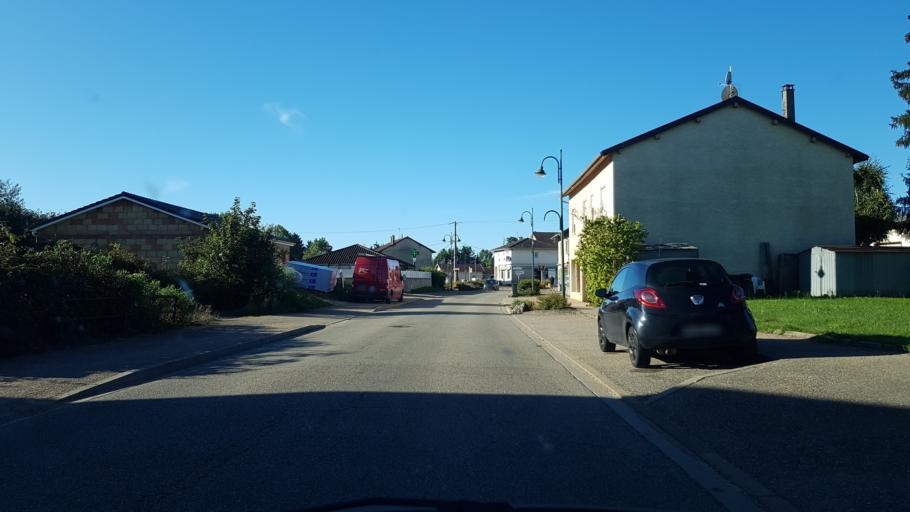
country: FR
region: Rhone-Alpes
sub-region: Departement de l'Ain
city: Villereversure
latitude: 46.1935
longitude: 5.3984
